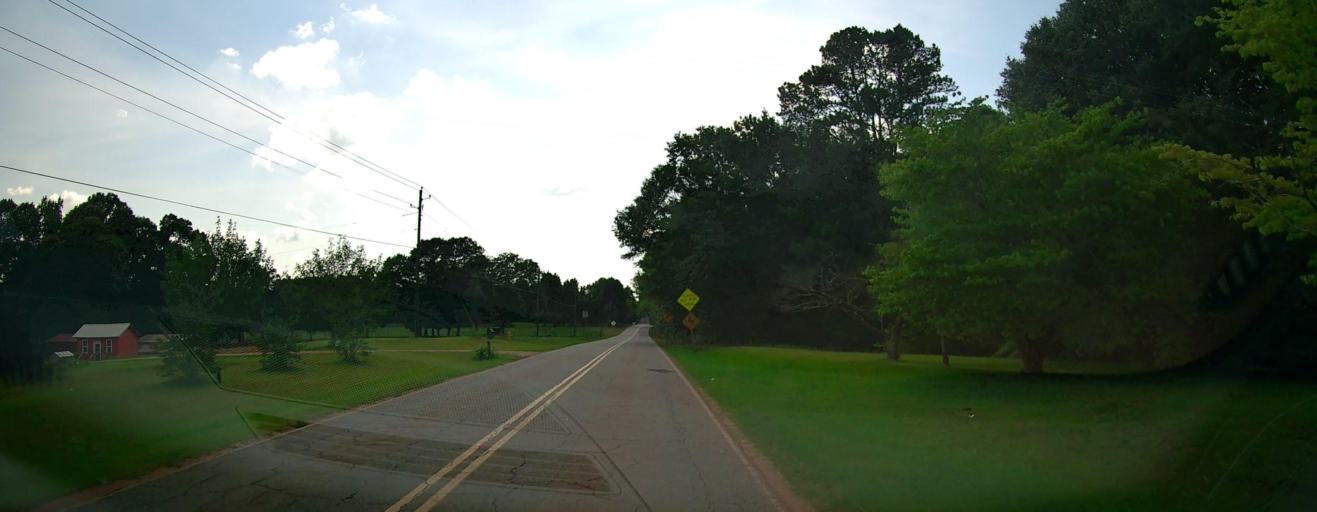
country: US
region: Georgia
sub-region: Spalding County
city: East Griffin
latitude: 33.2356
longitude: -84.1558
